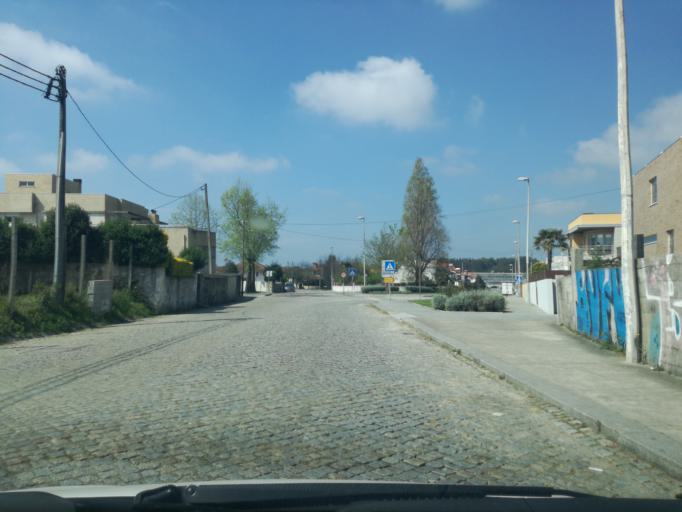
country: PT
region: Porto
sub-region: Maia
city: Gemunde
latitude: 41.2504
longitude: -8.6665
